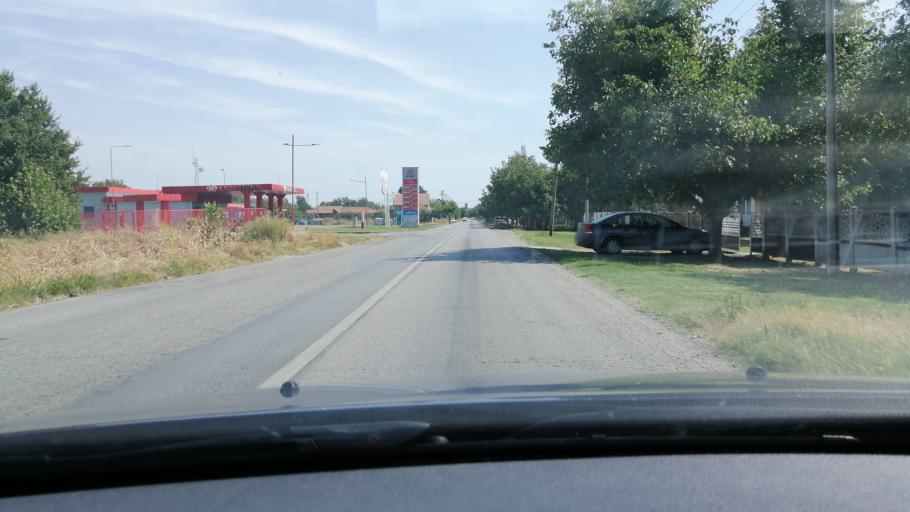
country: RS
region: Autonomna Pokrajina Vojvodina
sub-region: Srednjebanatski Okrug
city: Secanj
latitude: 45.3690
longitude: 20.7599
